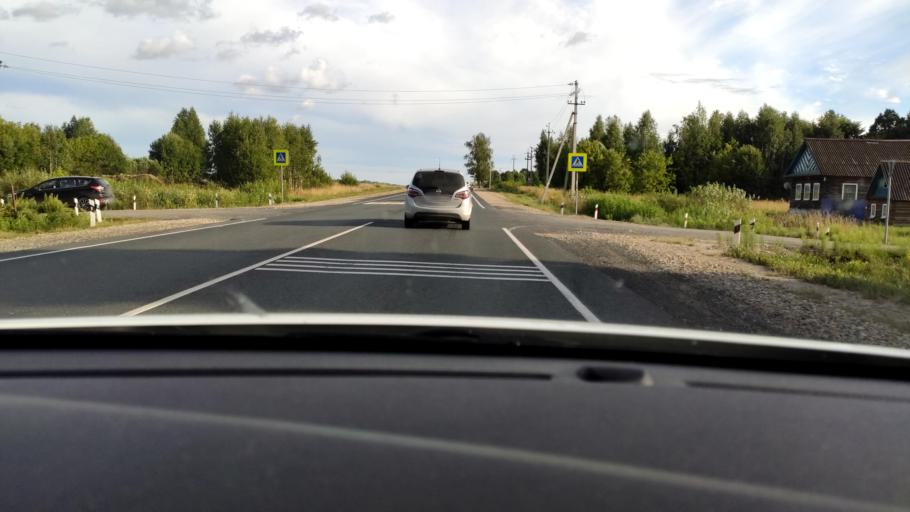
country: RU
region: Mariy-El
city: Suslonger
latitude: 56.2250
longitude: 48.2346
